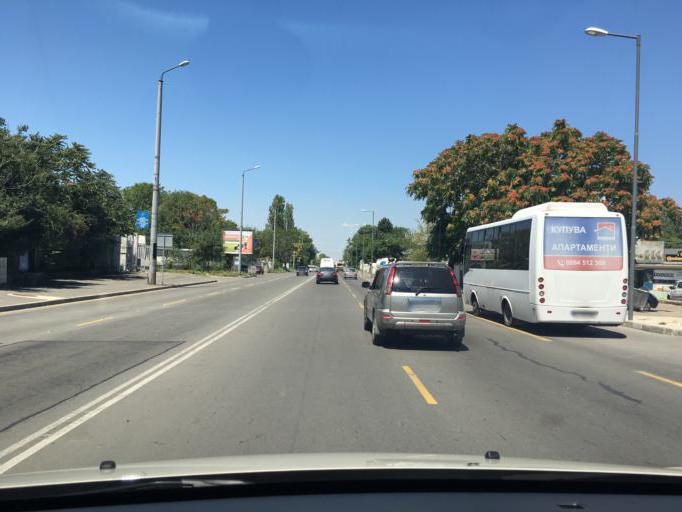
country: BG
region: Burgas
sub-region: Obshtina Burgas
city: Burgas
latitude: 42.4910
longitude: 27.4542
